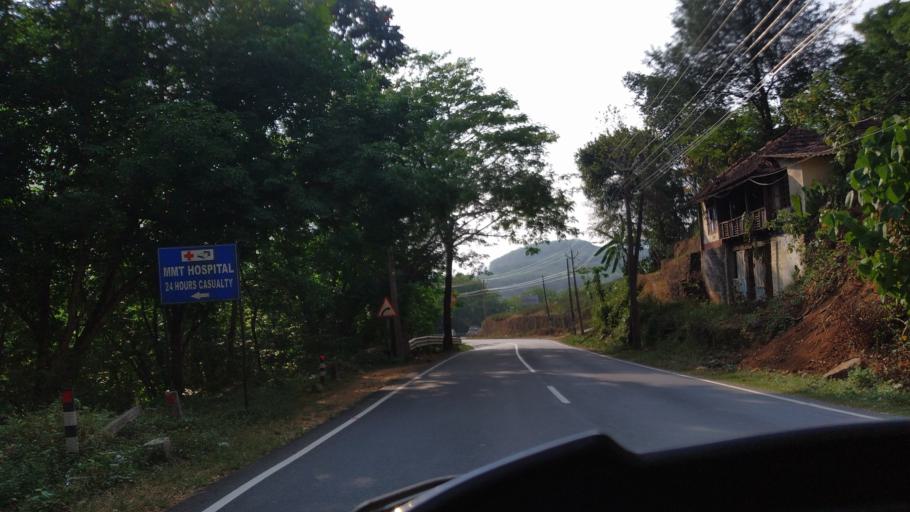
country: IN
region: Kerala
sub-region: Kottayam
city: Erattupetta
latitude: 9.5389
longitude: 76.9073
